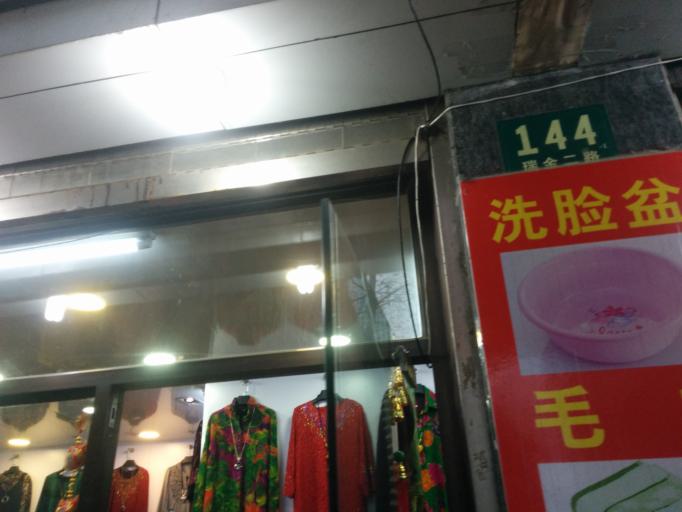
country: CN
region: Shanghai Shi
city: Luwan
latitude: 31.2122
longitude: 121.4616
